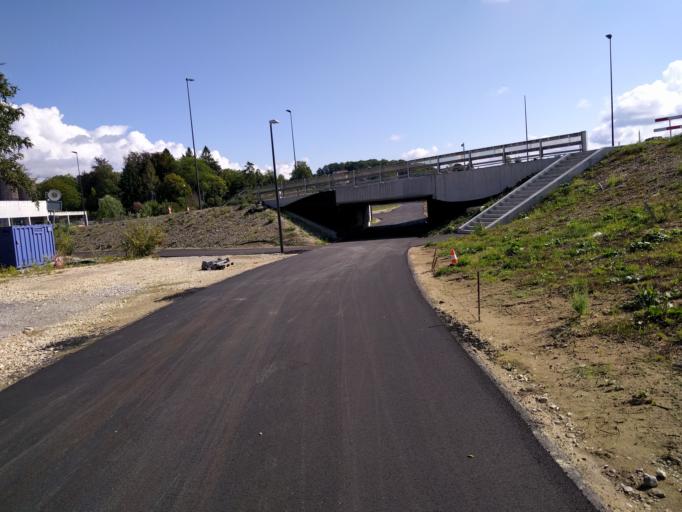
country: CH
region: Bern
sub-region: Biel/Bienne District
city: Brugg
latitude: 47.1236
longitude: 7.2599
